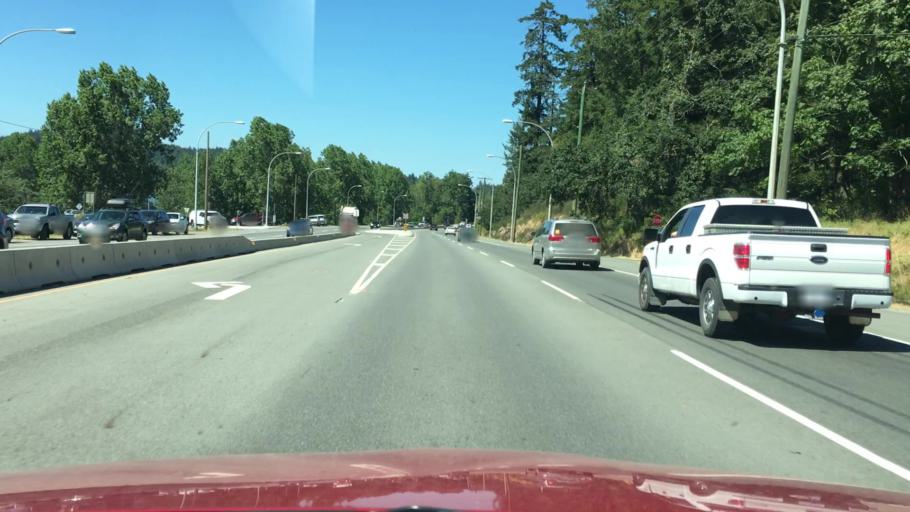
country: CA
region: British Columbia
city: Victoria
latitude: 48.5226
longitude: -123.3861
